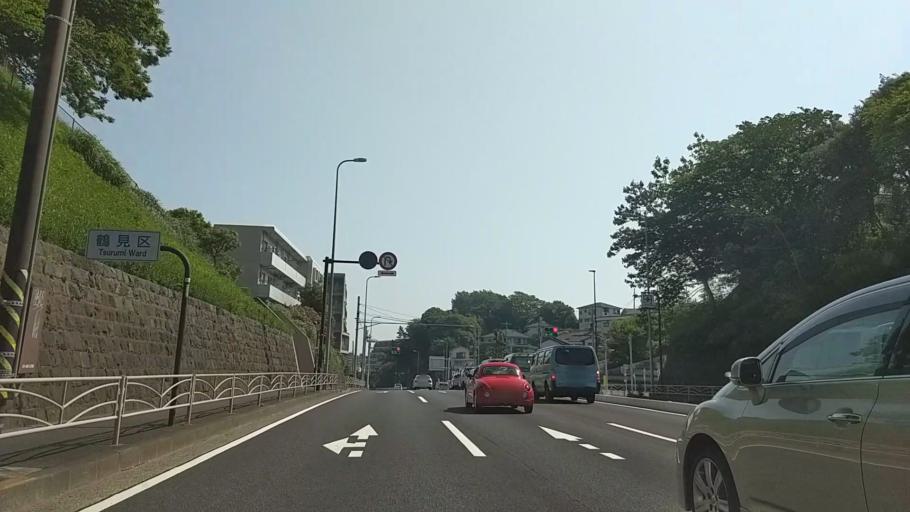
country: JP
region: Kanagawa
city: Yokohama
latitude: 35.4942
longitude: 139.6579
